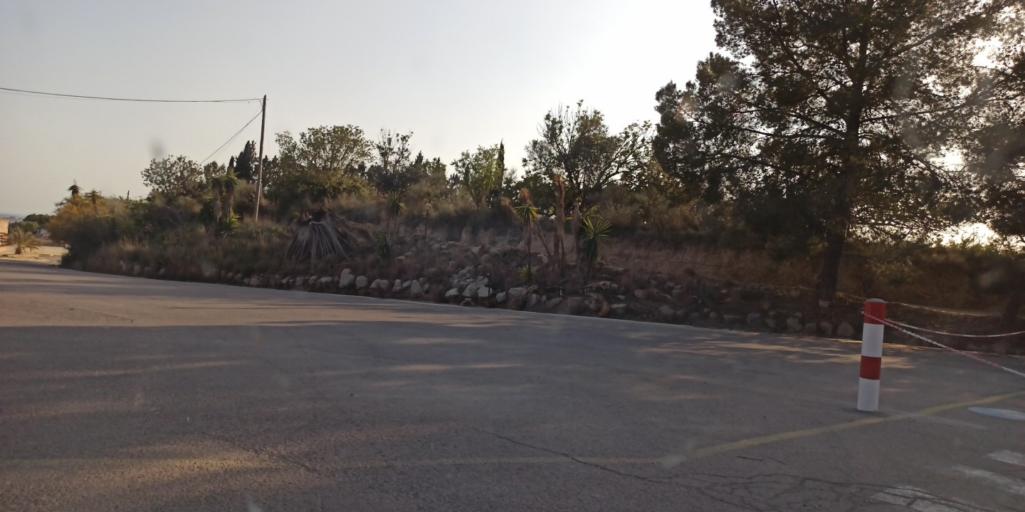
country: ES
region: Catalonia
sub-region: Provincia de Barcelona
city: Sant Feliu de Llobregat
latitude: 41.3988
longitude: 2.0543
